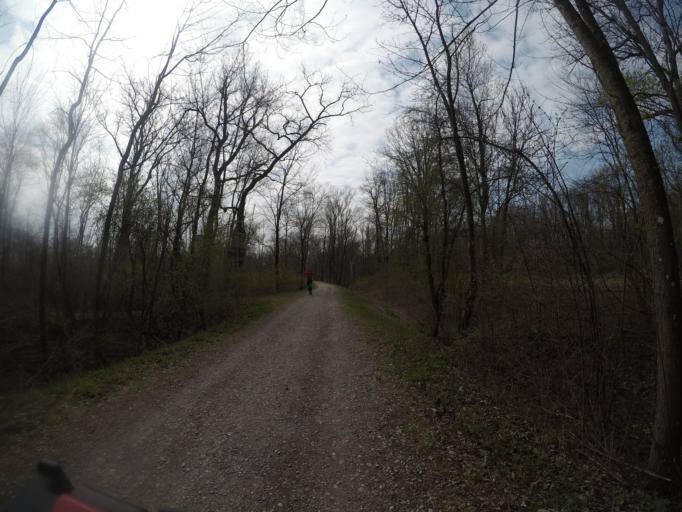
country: DE
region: Baden-Wuerttemberg
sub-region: Tuebingen Region
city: Ulm
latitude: 48.3770
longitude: 9.9713
